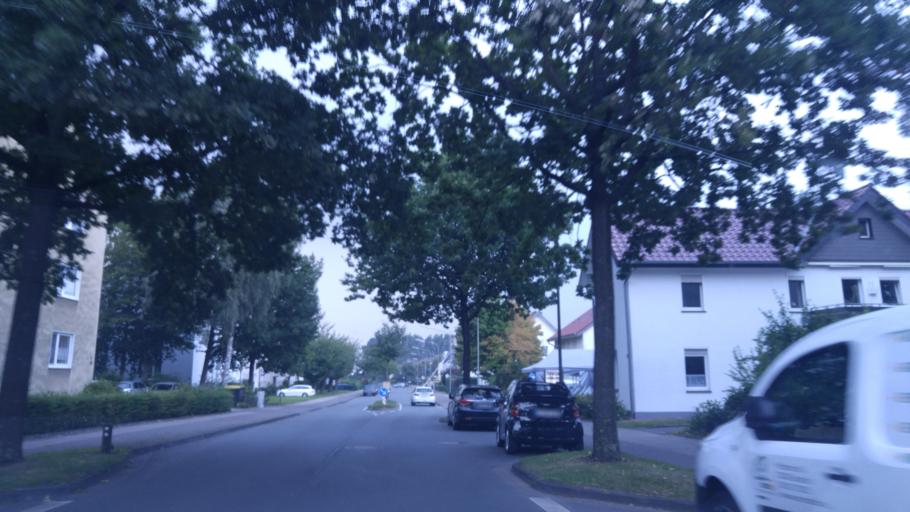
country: DE
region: North Rhine-Westphalia
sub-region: Regierungsbezirk Detmold
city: Bielefeld
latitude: 52.0490
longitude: 8.5276
